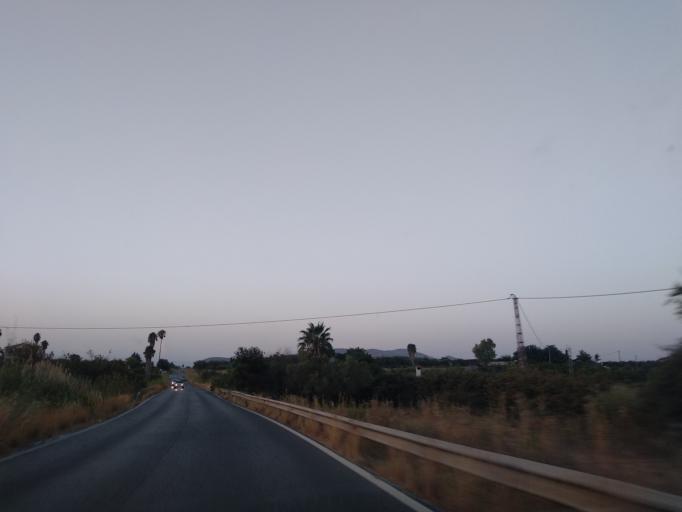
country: ES
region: Andalusia
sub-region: Provincia de Malaga
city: Alhaurin el Grande
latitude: 36.6658
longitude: -4.6685
